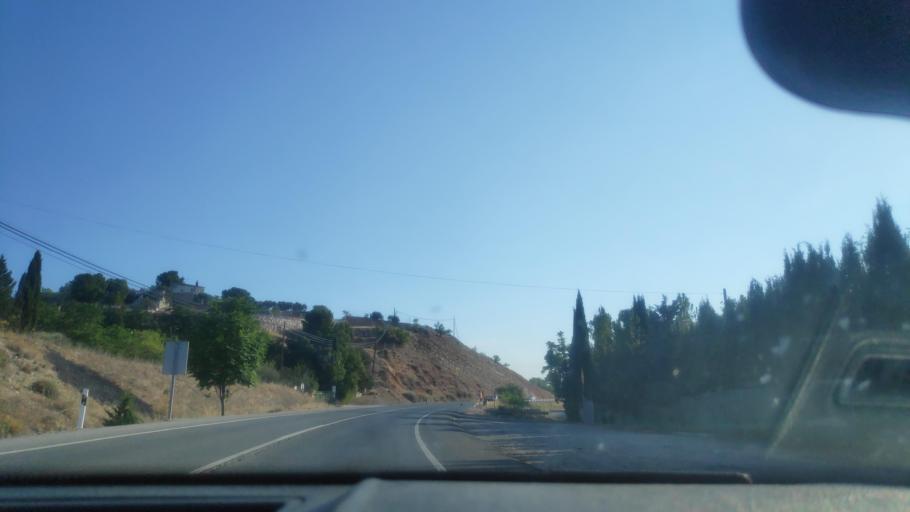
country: ES
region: Andalusia
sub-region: Provincia de Jaen
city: La Guardia de Jaen
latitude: 37.7811
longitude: -3.7315
